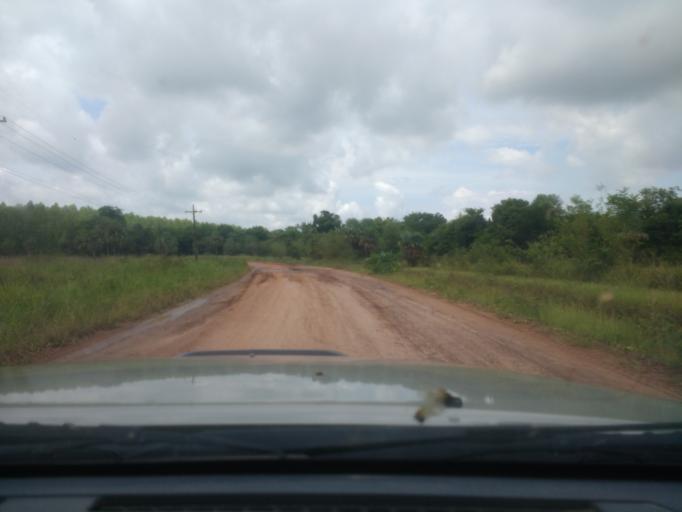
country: PY
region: San Pedro
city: Puerto Rosario
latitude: -24.3960
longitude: -57.1052
